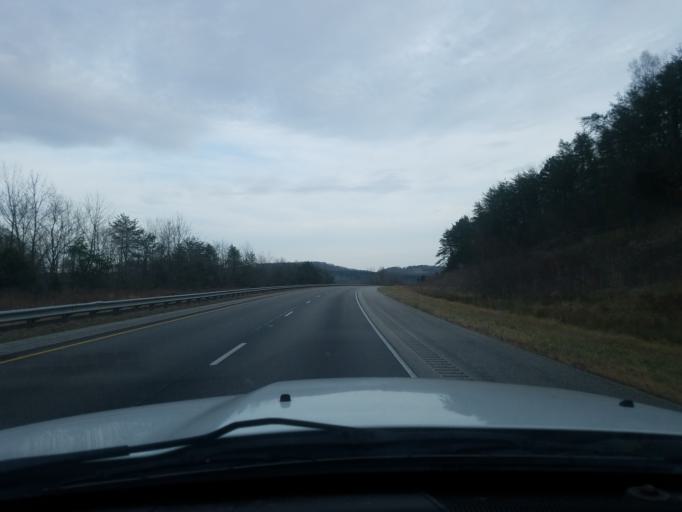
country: US
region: Indiana
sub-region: Crawford County
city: English
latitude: 38.2413
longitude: -86.5423
